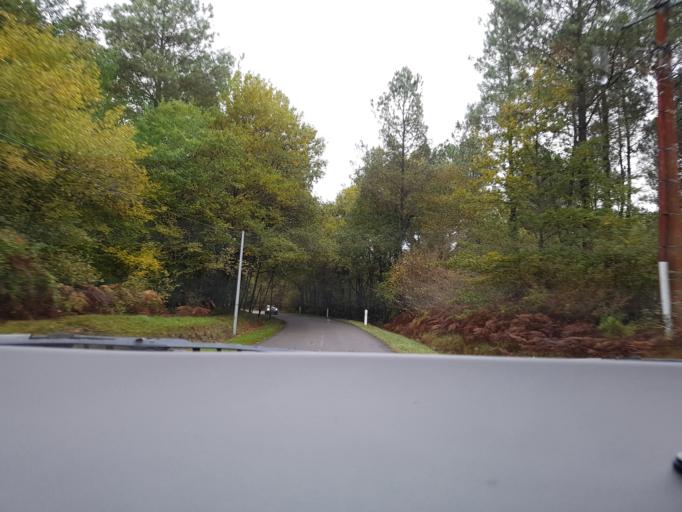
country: FR
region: Aquitaine
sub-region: Departement des Landes
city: Roquefort
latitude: 44.0527
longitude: -0.3430
